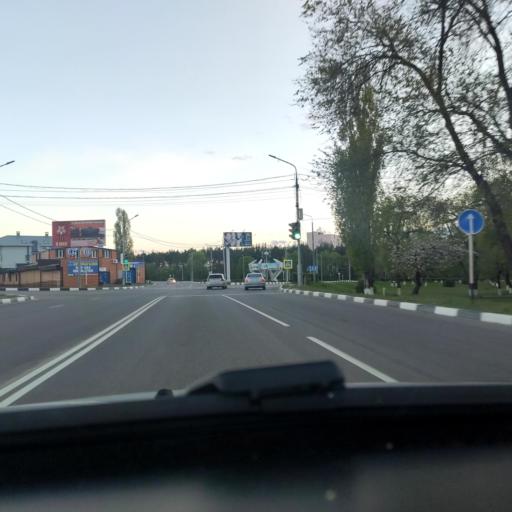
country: RU
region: Voronezj
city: Novovoronezh
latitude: 51.3164
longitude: 39.2202
